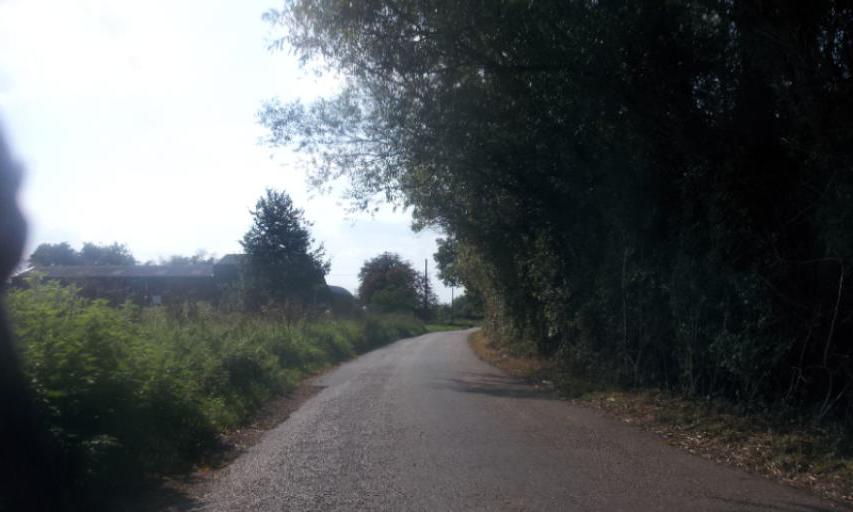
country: GB
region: England
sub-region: Kent
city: Yalding
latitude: 51.1994
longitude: 0.4475
